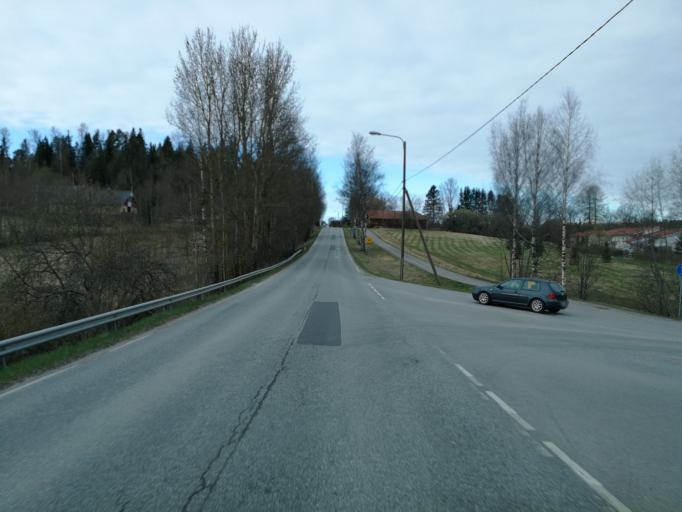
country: FI
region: Varsinais-Suomi
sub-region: Salo
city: Muurla
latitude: 60.3553
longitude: 23.2877
